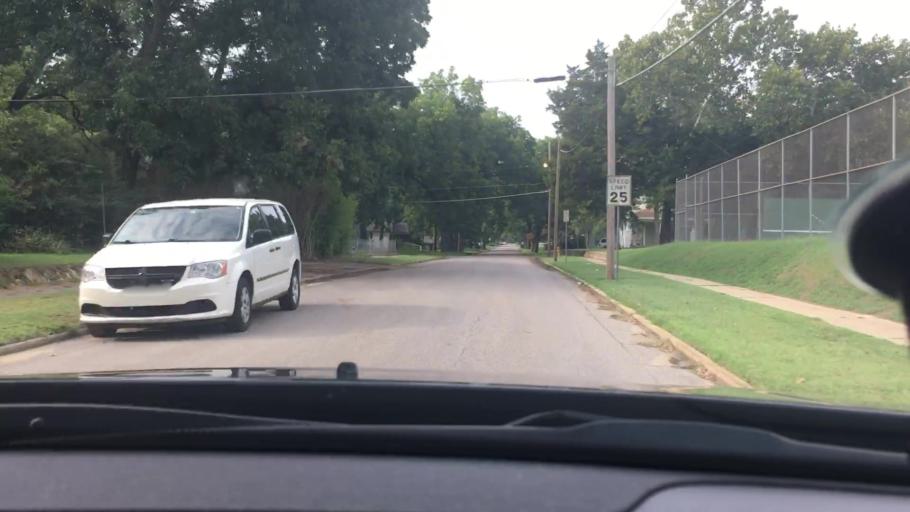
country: US
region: Oklahoma
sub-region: Carter County
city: Ardmore
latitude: 34.1831
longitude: -97.1278
